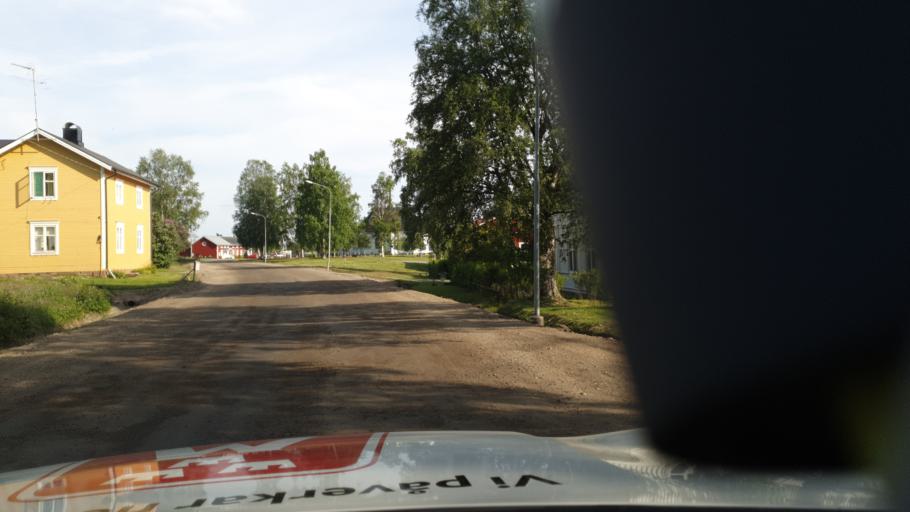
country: SE
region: Vaesterbotten
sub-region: Robertsfors Kommun
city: Robertsfors
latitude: 64.2831
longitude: 21.0369
